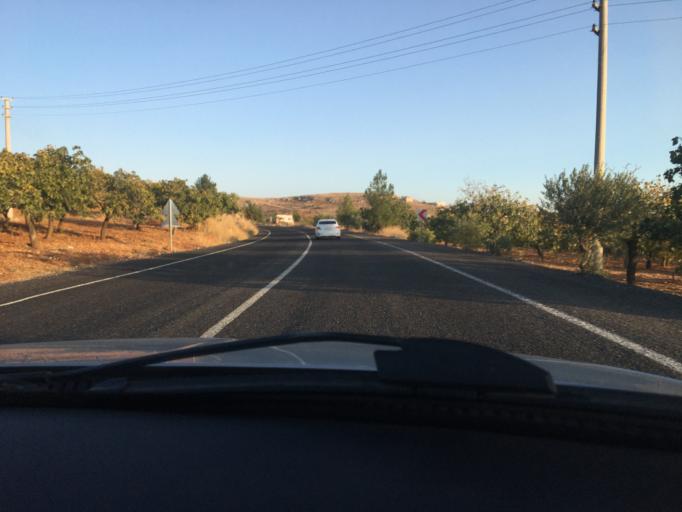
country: TR
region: Sanliurfa
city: Halfeti
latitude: 37.2162
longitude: 37.9562
